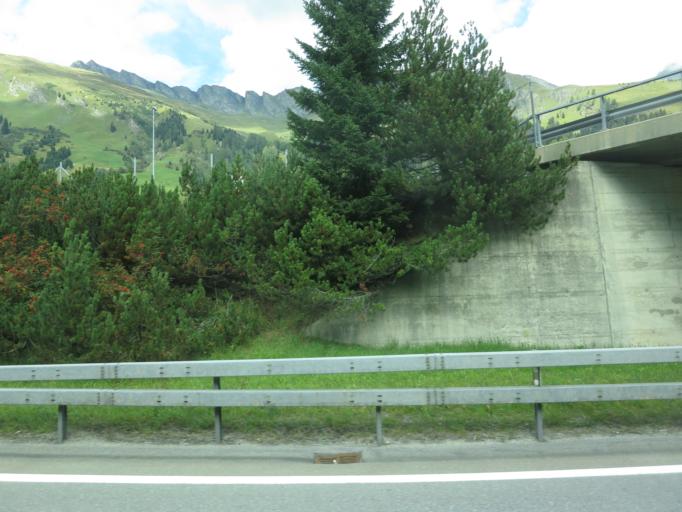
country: CH
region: Grisons
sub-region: Hinterrhein District
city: Hinterrhein
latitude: 46.5444
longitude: 9.2961
